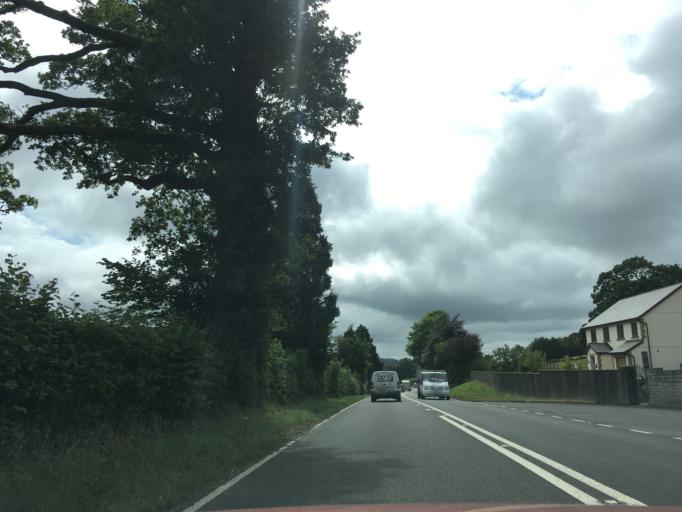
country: GB
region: Wales
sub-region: Carmarthenshire
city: Llangathen
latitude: 51.8847
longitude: -4.0658
